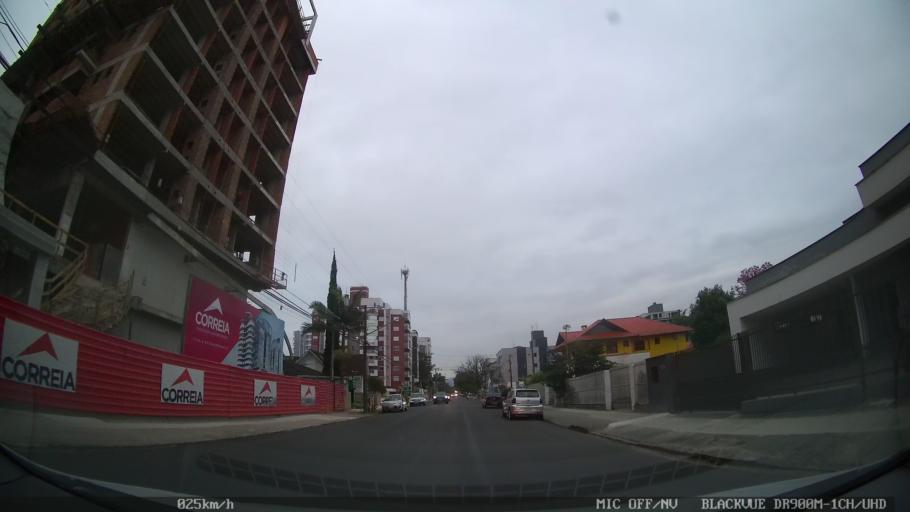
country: BR
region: Santa Catarina
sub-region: Joinville
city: Joinville
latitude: -26.2777
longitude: -48.8515
